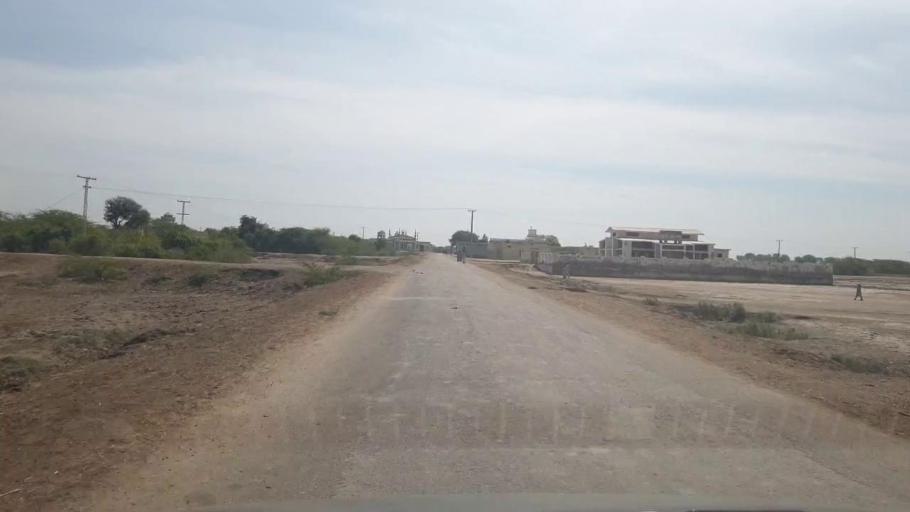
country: PK
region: Sindh
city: Umarkot
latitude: 25.3321
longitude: 69.5930
